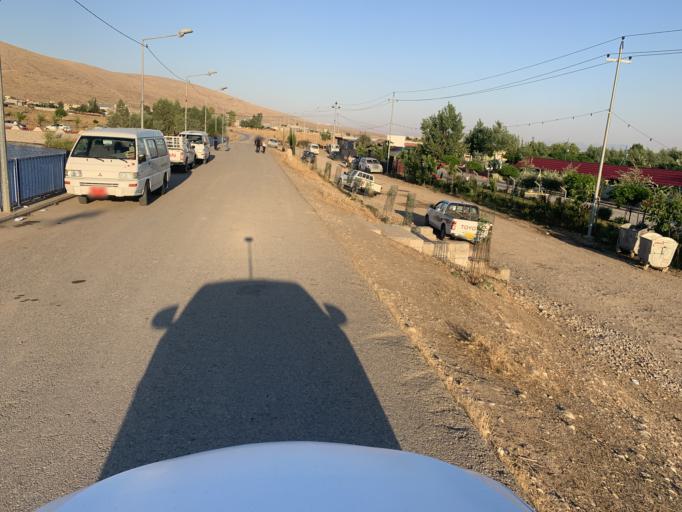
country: IQ
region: As Sulaymaniyah
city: Raniye
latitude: 36.2718
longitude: 44.7539
